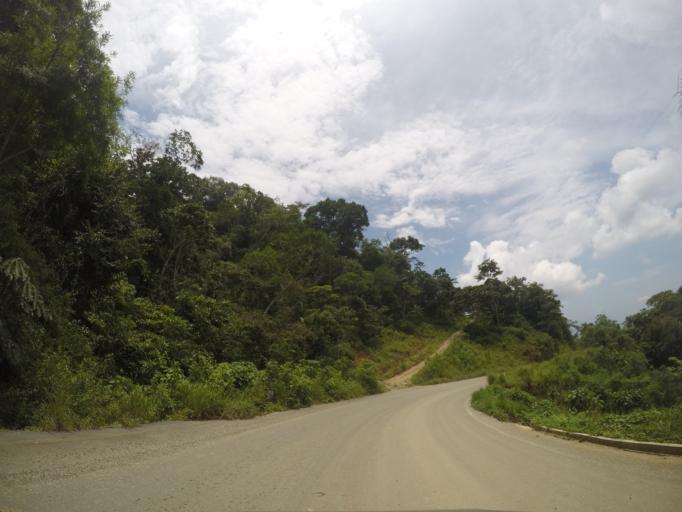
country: MX
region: Oaxaca
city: Pluma Hidalgo
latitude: 15.9100
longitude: -96.4193
